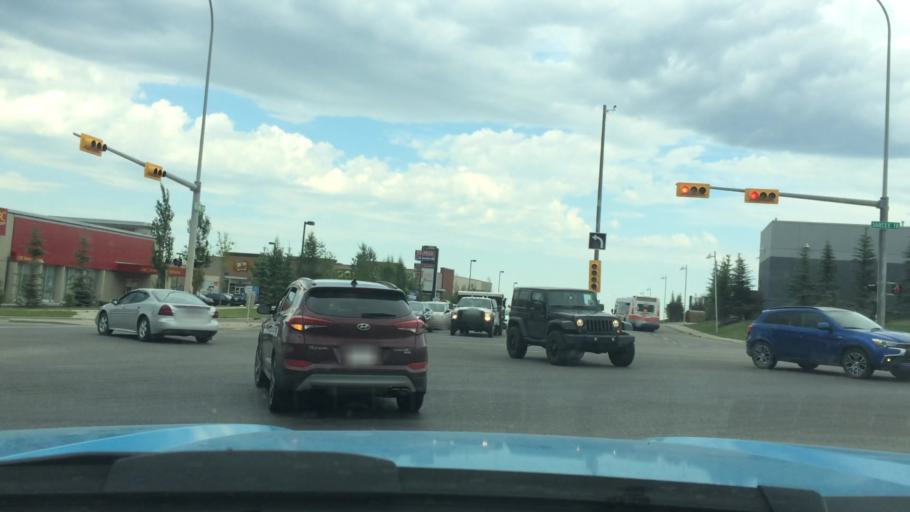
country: CA
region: Alberta
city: Calgary
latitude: 51.1599
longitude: -114.1628
